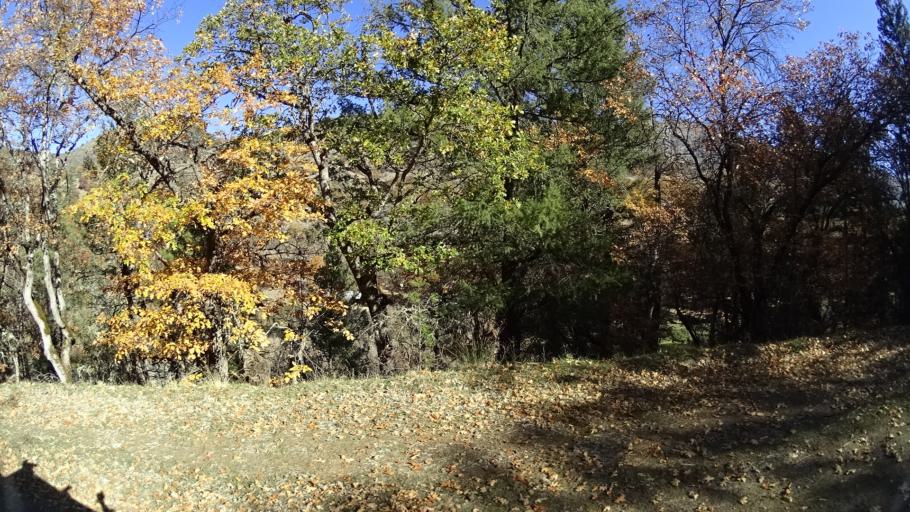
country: US
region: California
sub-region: Siskiyou County
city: Yreka
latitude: 41.8667
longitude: -122.8073
